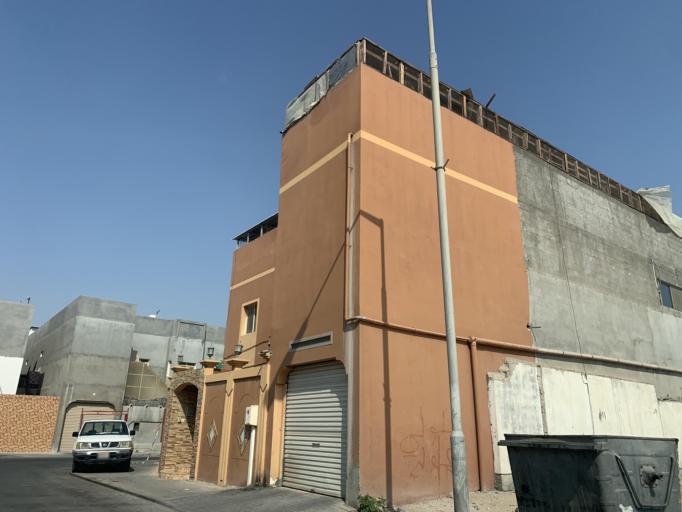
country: BH
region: Central Governorate
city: Madinat Hamad
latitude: 26.1227
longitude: 50.4927
